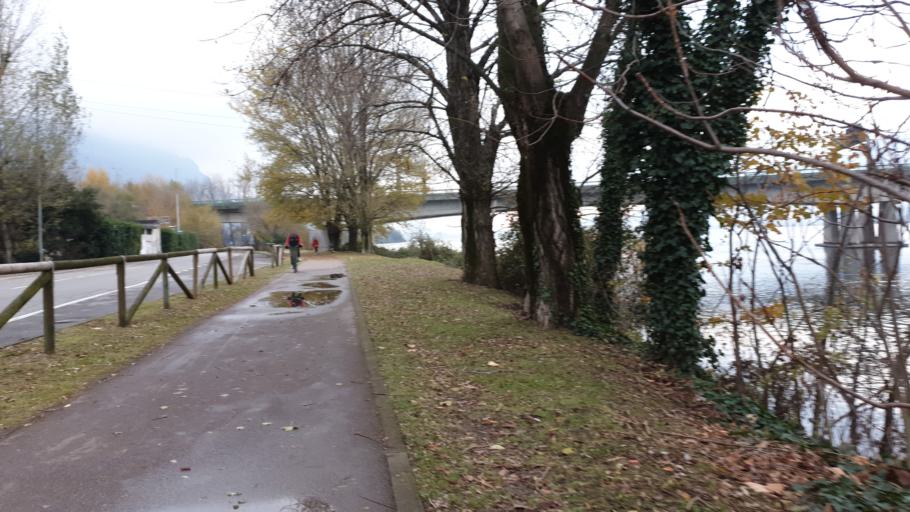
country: IT
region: Lombardy
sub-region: Provincia di Lecco
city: Pescate
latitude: 45.8402
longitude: 9.3999
